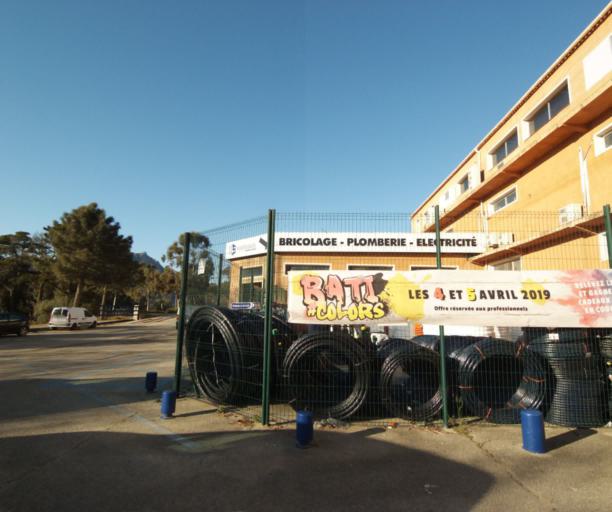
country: FR
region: Corsica
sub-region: Departement de la Corse-du-Sud
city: Propriano
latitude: 41.6676
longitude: 8.9187
